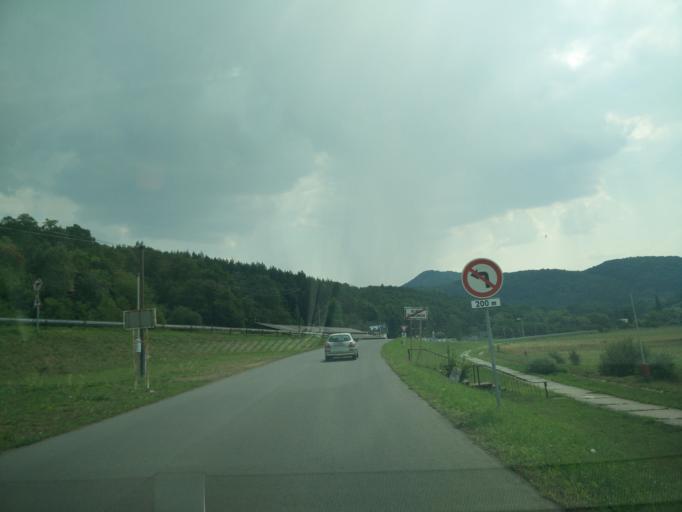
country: SK
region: Banskobystricky
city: Zarnovica
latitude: 48.5366
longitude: 18.7779
